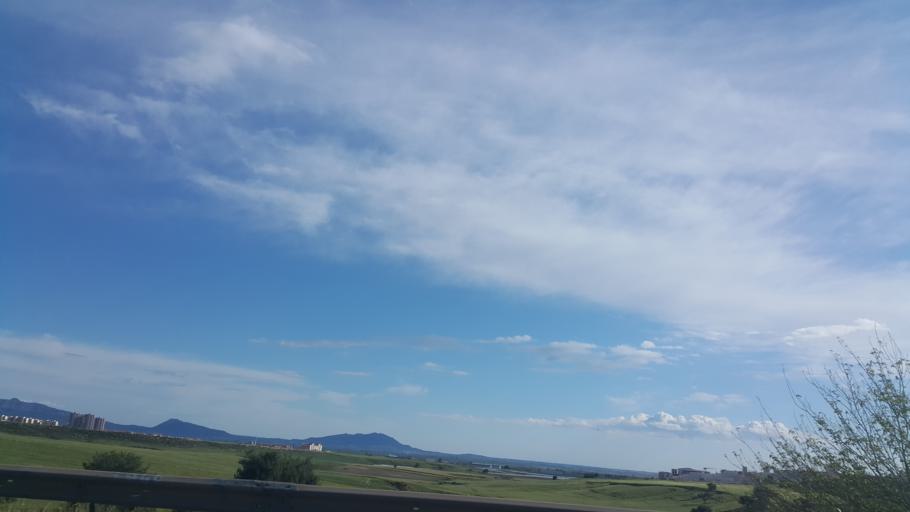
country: TR
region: Adana
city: Yakapinar
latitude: 36.9998
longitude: 35.5575
